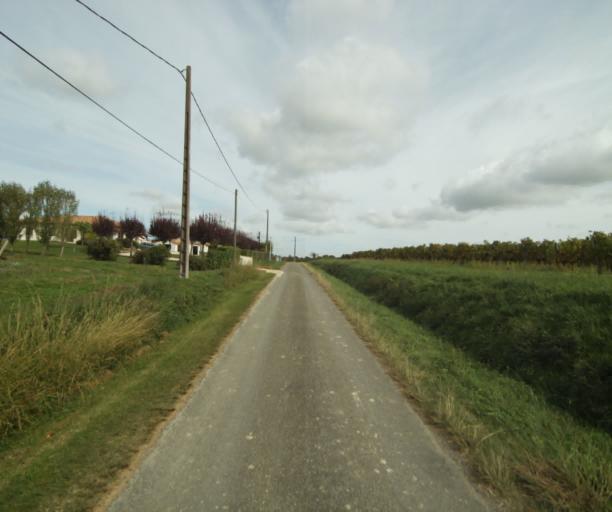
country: FR
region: Midi-Pyrenees
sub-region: Departement du Gers
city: Eauze
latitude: 43.8289
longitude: 0.1212
